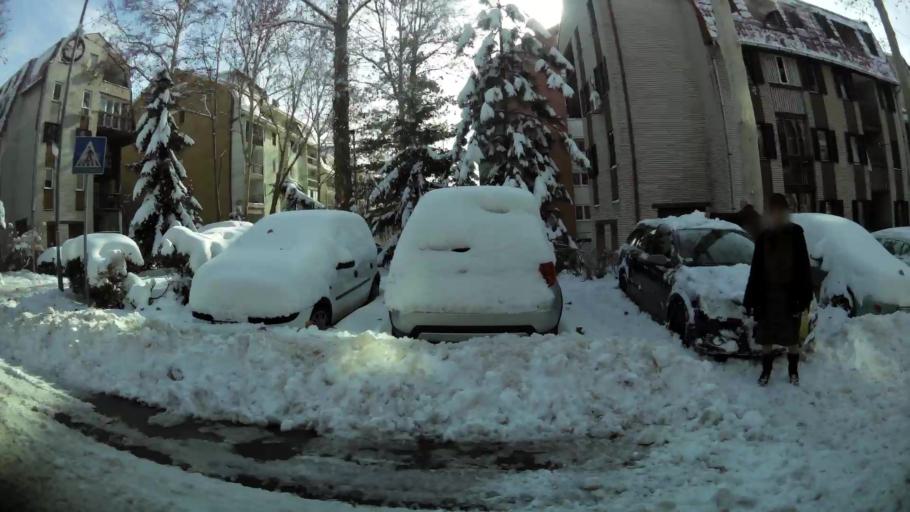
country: RS
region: Central Serbia
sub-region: Belgrade
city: Zvezdara
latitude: 44.7874
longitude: 20.5389
